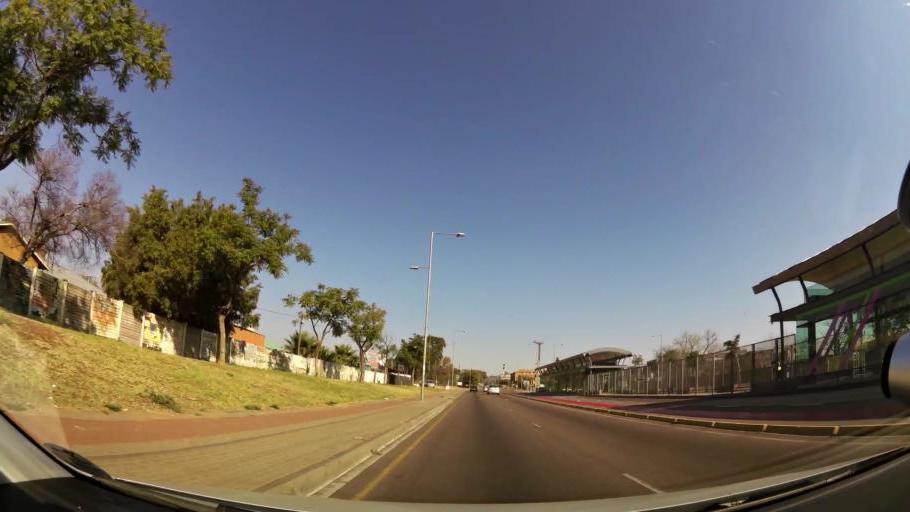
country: ZA
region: Gauteng
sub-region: City of Tshwane Metropolitan Municipality
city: Pretoria
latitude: -25.7068
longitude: 28.1870
